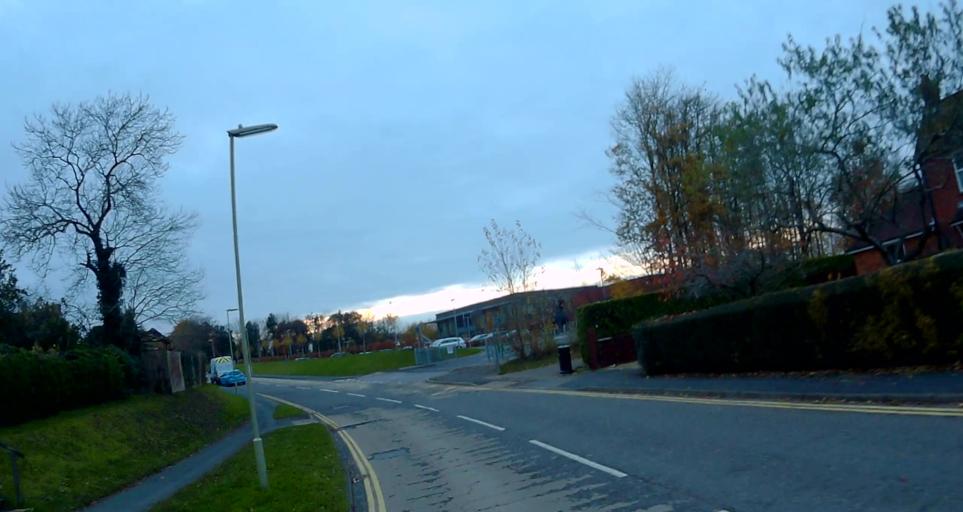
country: GB
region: England
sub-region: Hampshire
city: Odiham
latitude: 51.2531
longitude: -0.9497
